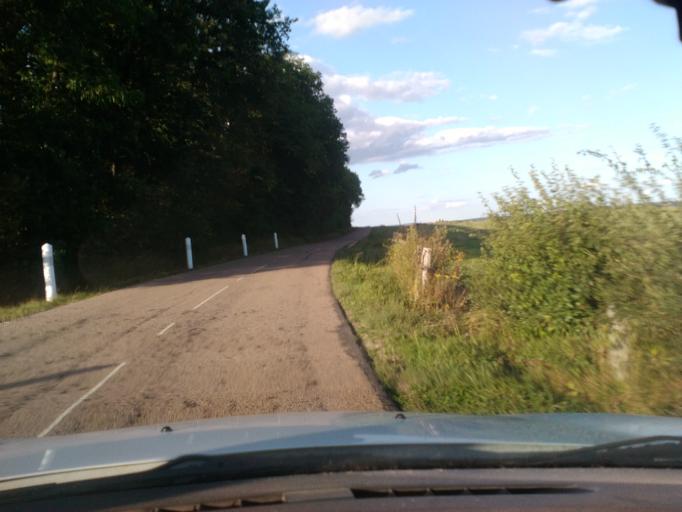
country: FR
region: Lorraine
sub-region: Departement des Vosges
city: Mirecourt
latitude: 48.3491
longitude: 6.0389
